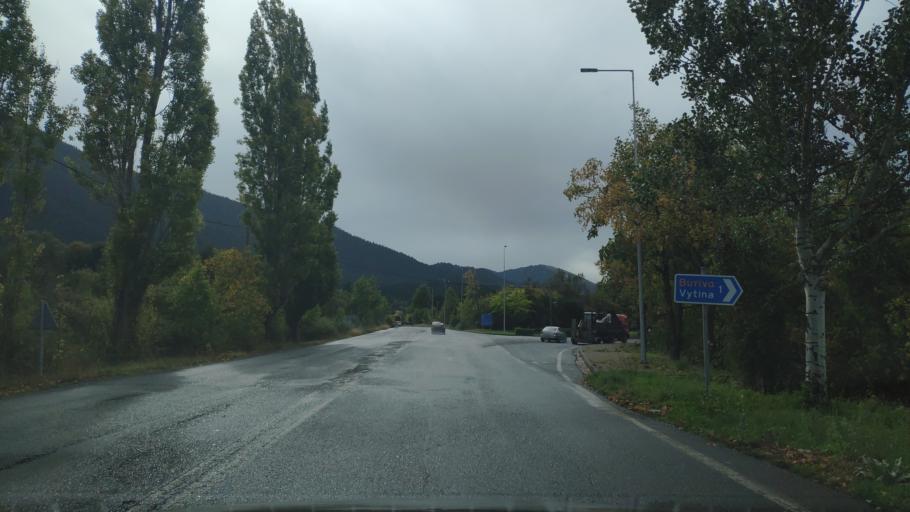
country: GR
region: Peloponnese
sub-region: Nomos Arkadias
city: Langadhia
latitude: 37.6748
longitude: 22.1924
